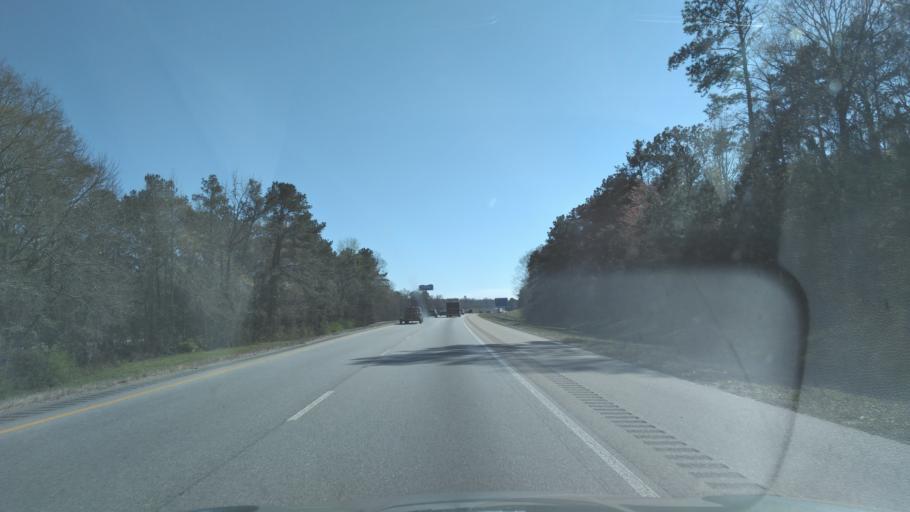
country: US
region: Alabama
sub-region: Lowndes County
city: Fort Deposit
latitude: 31.9967
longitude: -86.5254
